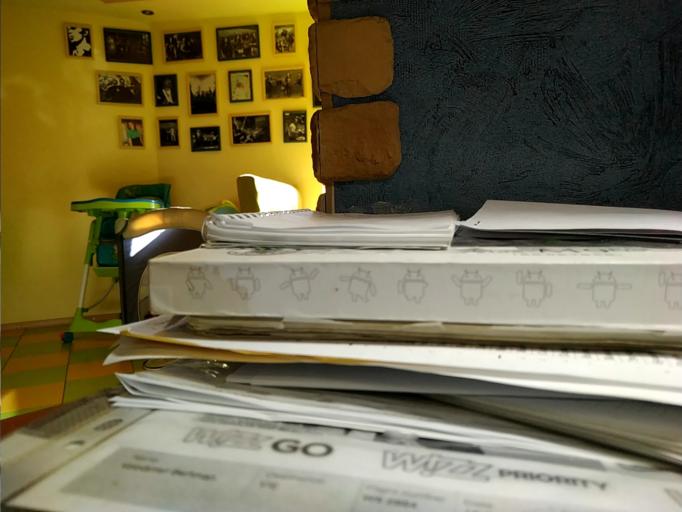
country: RU
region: Novgorod
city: Poddor'ye
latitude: 57.5942
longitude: 30.8148
